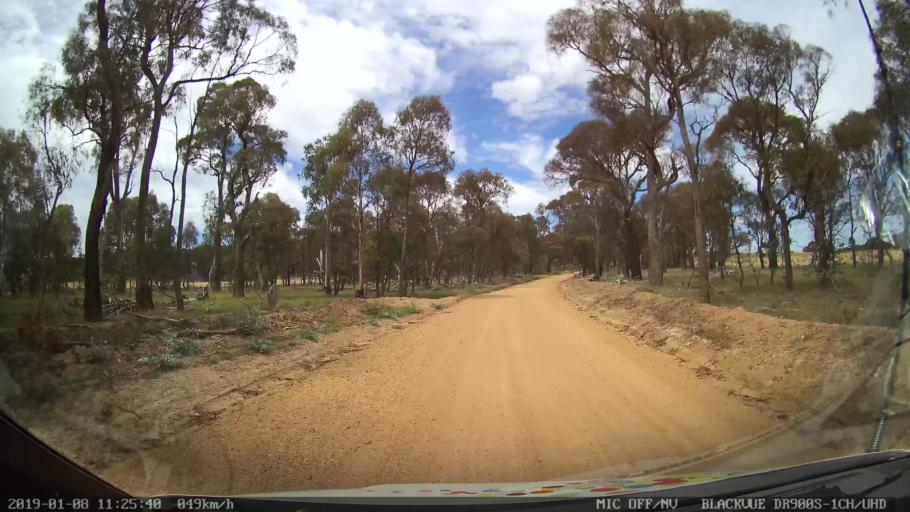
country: AU
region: New South Wales
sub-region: Guyra
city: Guyra
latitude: -30.2752
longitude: 151.5612
